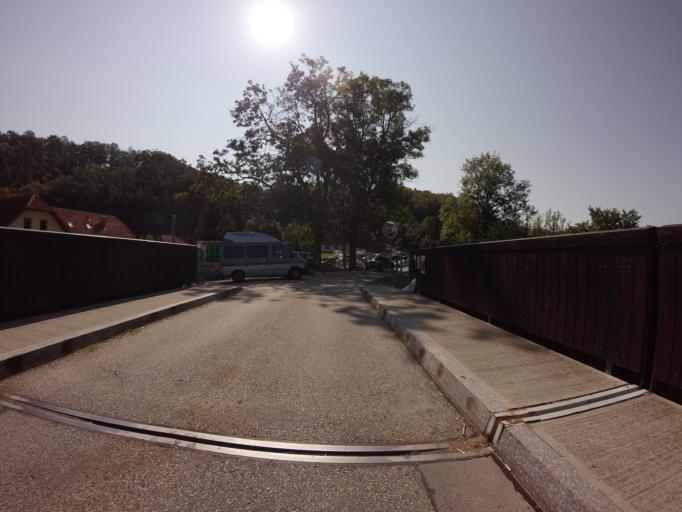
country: CZ
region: Jihocesky
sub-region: Okres Cesky Krumlov
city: Cesky Krumlov
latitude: 48.8529
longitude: 14.3707
